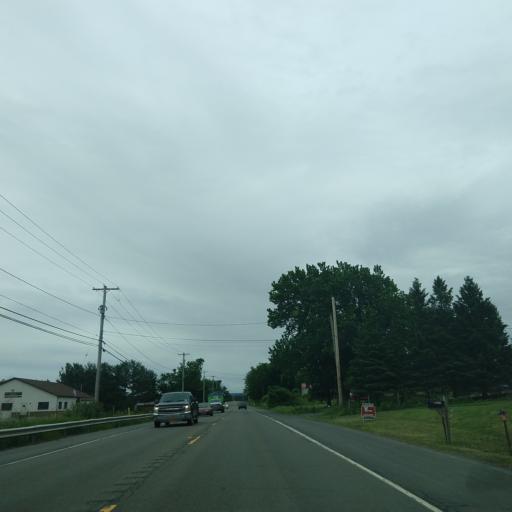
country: US
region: New York
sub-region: Tompkins County
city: Dryden
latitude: 42.4831
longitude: -76.3625
